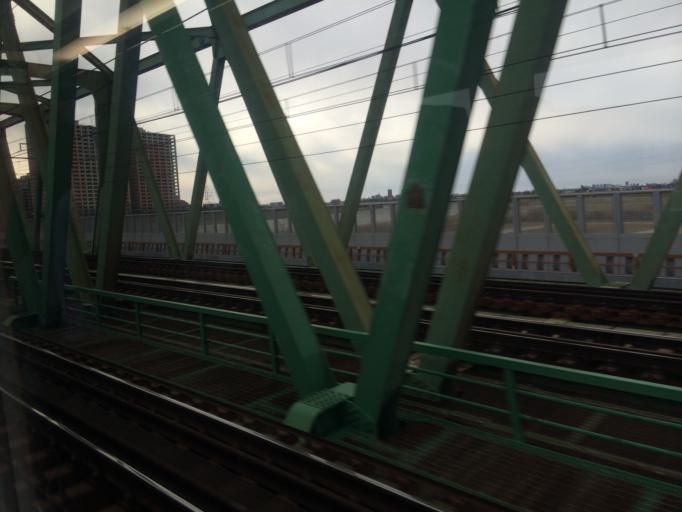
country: JP
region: Chiba
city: Matsudo
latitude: 35.7339
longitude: 139.8961
